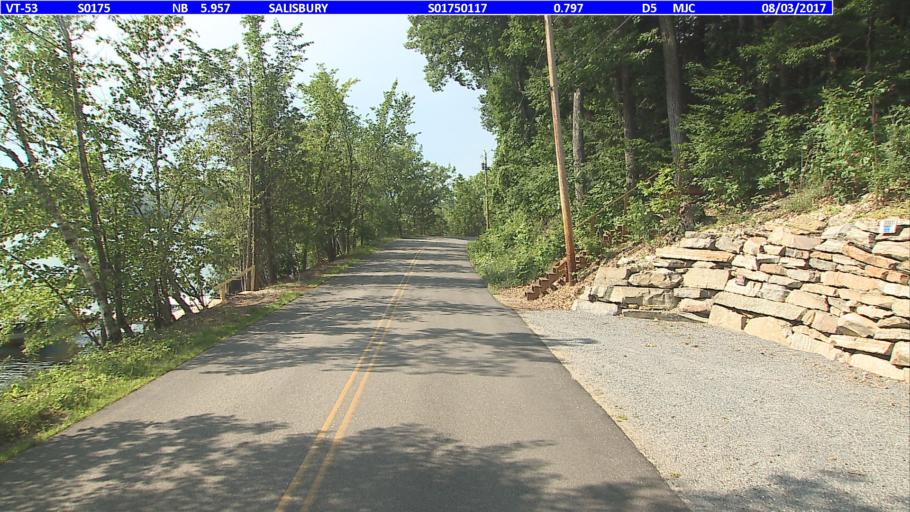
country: US
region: Vermont
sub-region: Rutland County
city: Brandon
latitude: 43.9092
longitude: -73.0665
